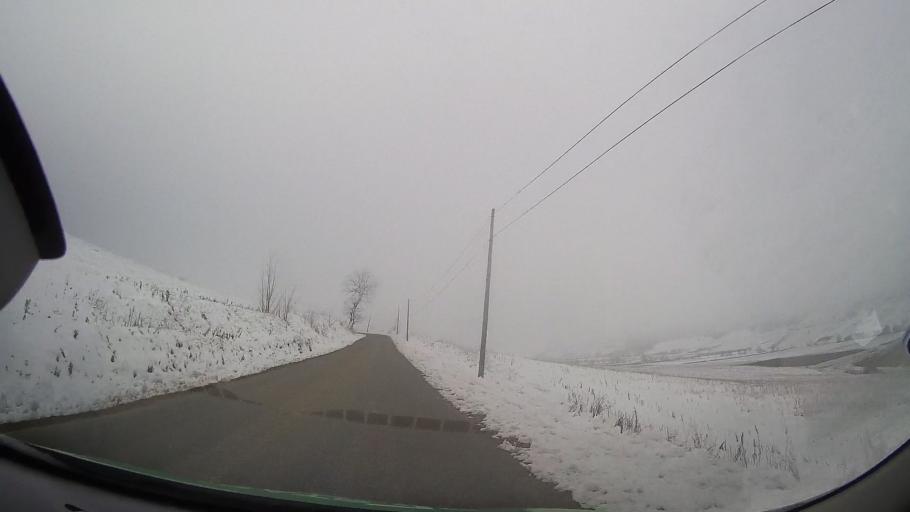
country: RO
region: Bacau
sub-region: Comuna Stanisesti
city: Stanisesti
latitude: 46.4126
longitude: 27.2697
